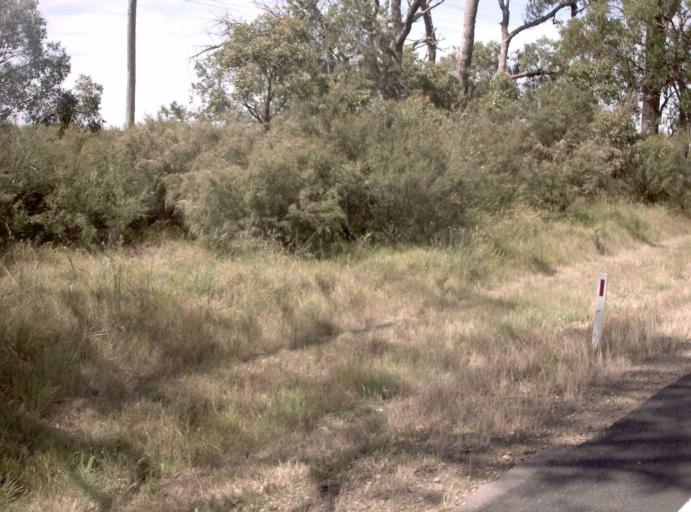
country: AU
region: Victoria
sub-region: Wellington
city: Sale
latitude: -37.9343
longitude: 147.1753
